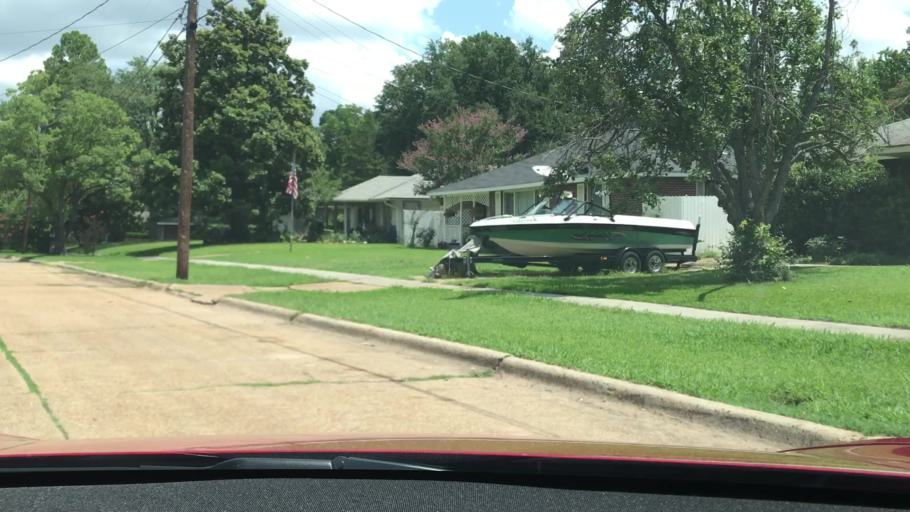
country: US
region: Louisiana
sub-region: Bossier Parish
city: Bossier City
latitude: 32.4572
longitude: -93.7259
